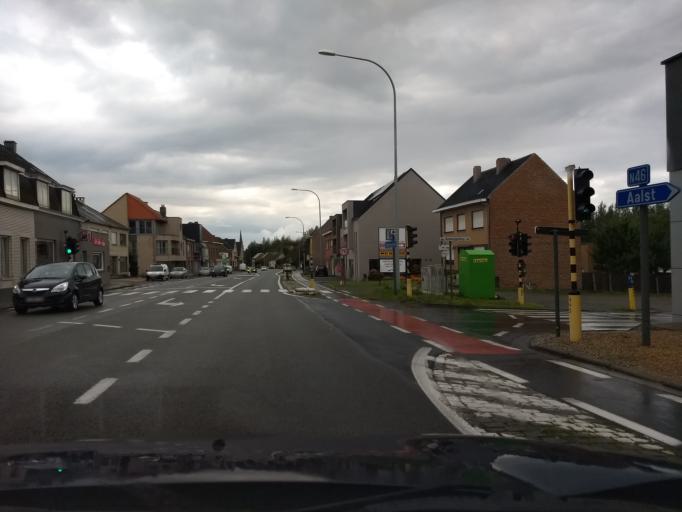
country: BE
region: Flanders
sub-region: Provincie Oost-Vlaanderen
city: Herzele
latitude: 50.9170
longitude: 3.9306
